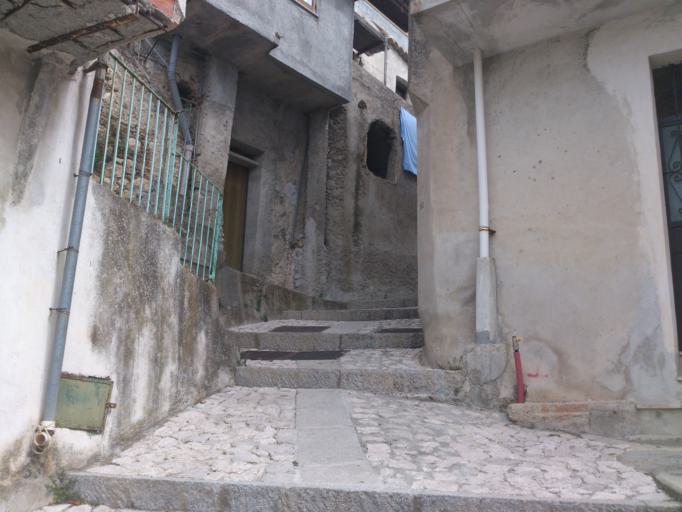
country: IT
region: Calabria
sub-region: Provincia di Reggio Calabria
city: Stilo
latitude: 38.4785
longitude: 16.4675
